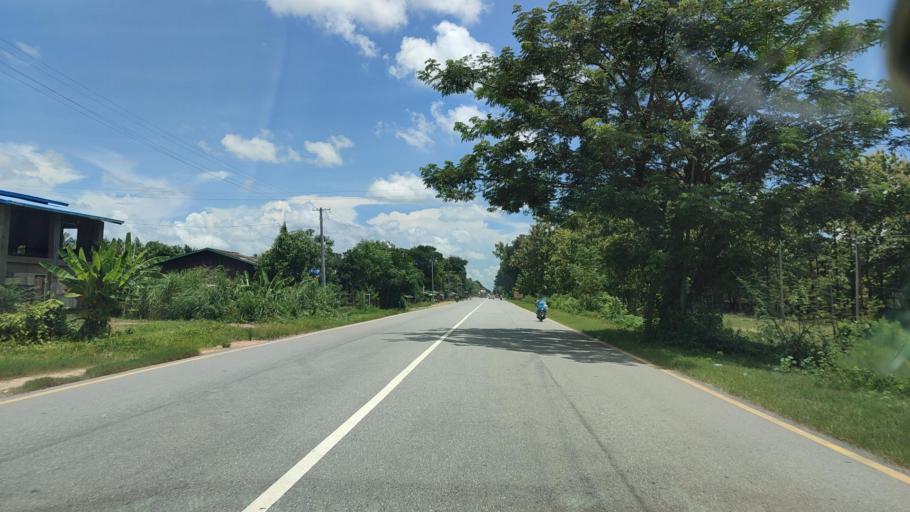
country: MM
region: Bago
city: Pyu
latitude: 18.4212
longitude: 96.4532
